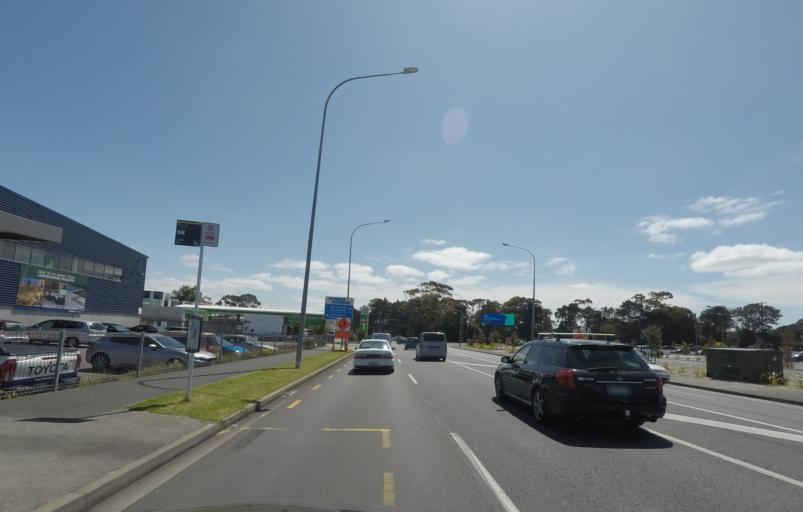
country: NZ
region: Auckland
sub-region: Auckland
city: Tamaki
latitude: -36.8891
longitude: 174.8324
